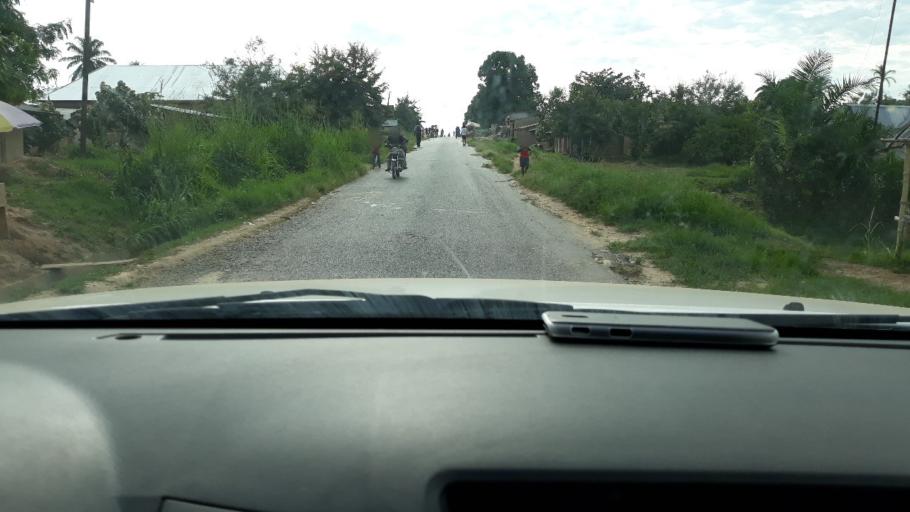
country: CD
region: Maniema
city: Kindu
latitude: -2.9515
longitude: 25.9455
